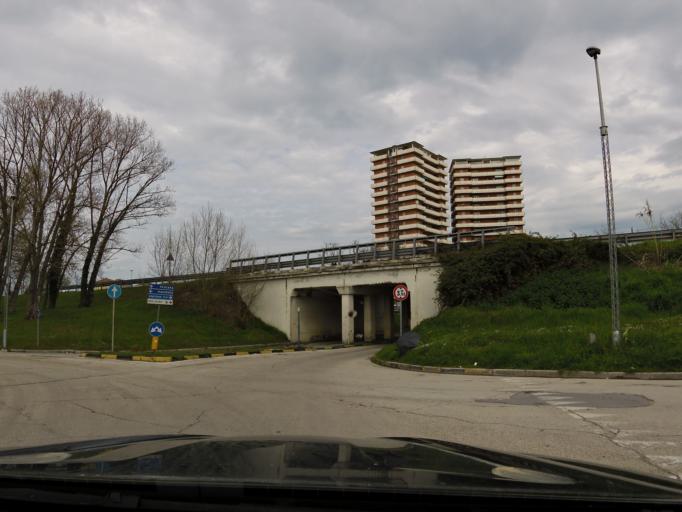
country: IT
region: The Marches
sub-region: Provincia di Macerata
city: Porto Recanati
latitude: 43.4197
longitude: 13.6652
